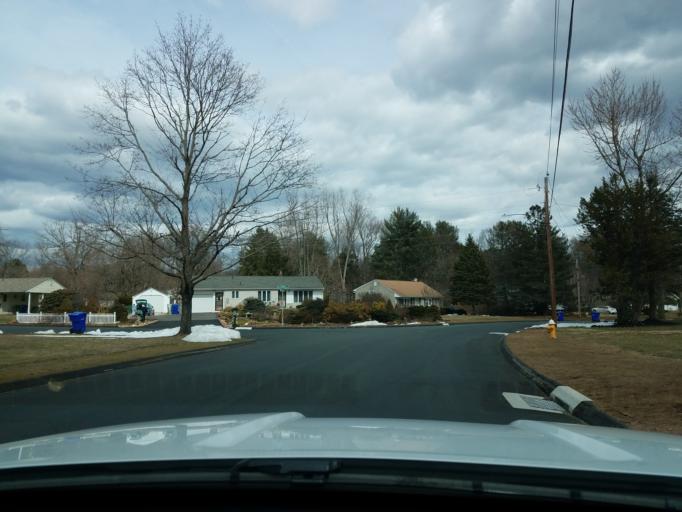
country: US
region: Connecticut
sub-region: Hartford County
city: Manchester
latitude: 41.8257
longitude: -72.5168
